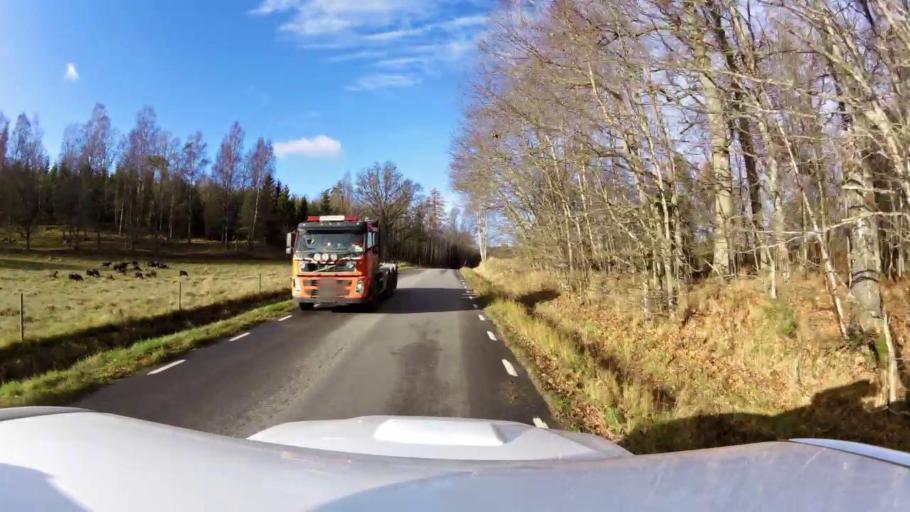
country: SE
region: OEstergoetland
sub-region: Linkopings Kommun
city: Sturefors
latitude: 58.3166
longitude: 15.6669
